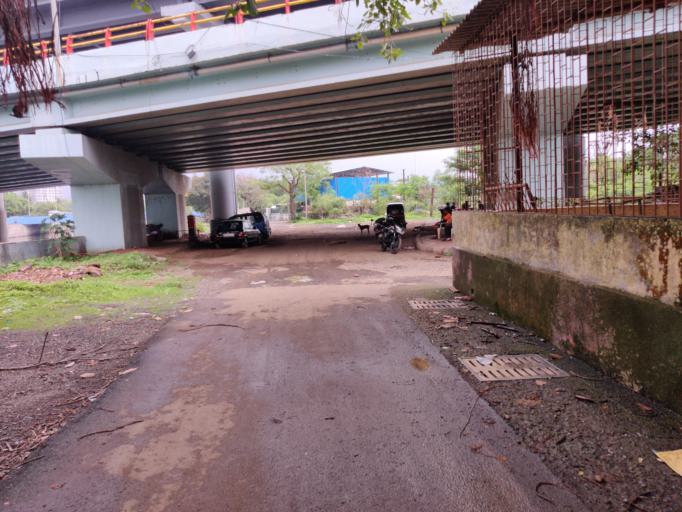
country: IN
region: Maharashtra
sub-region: Mumbai Suburban
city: Borivli
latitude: 19.2583
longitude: 72.8562
